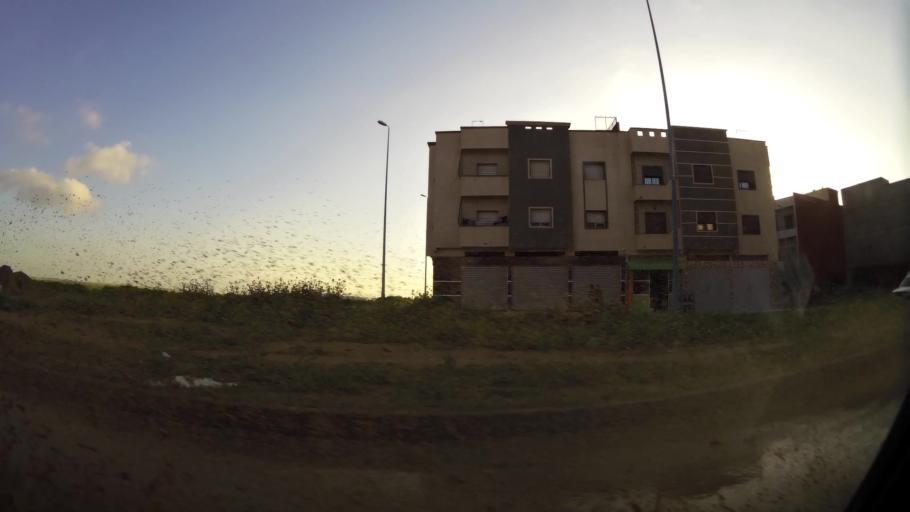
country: MA
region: Chaouia-Ouardigha
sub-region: Settat Province
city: Settat
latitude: 32.9859
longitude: -7.5999
